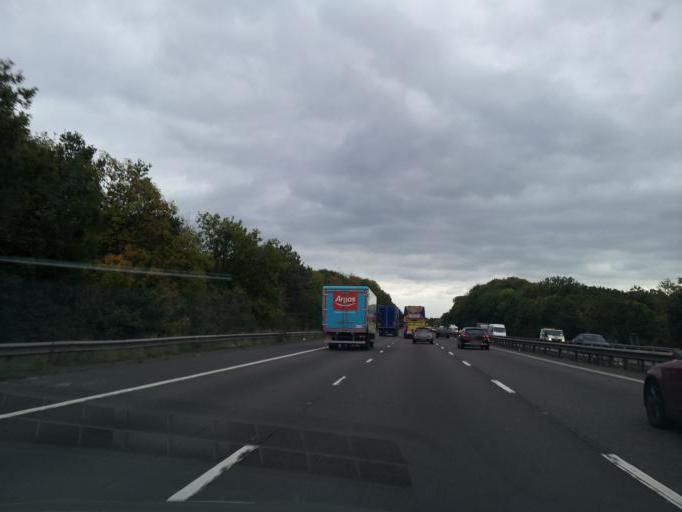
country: GB
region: England
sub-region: Northamptonshire
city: Hartwell
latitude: 52.1466
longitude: -0.8400
